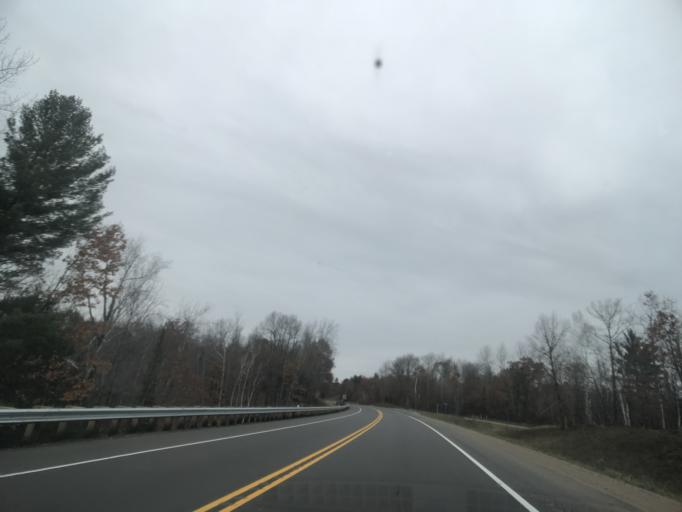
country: US
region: Wisconsin
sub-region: Menominee County
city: Legend Lake
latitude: 45.2716
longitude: -88.5087
